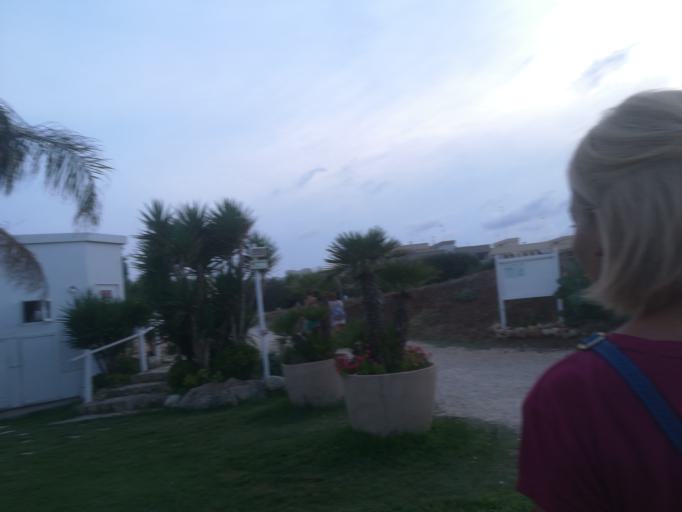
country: IT
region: Apulia
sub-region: Provincia di Bari
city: Monopoli
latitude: 40.9456
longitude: 17.3098
